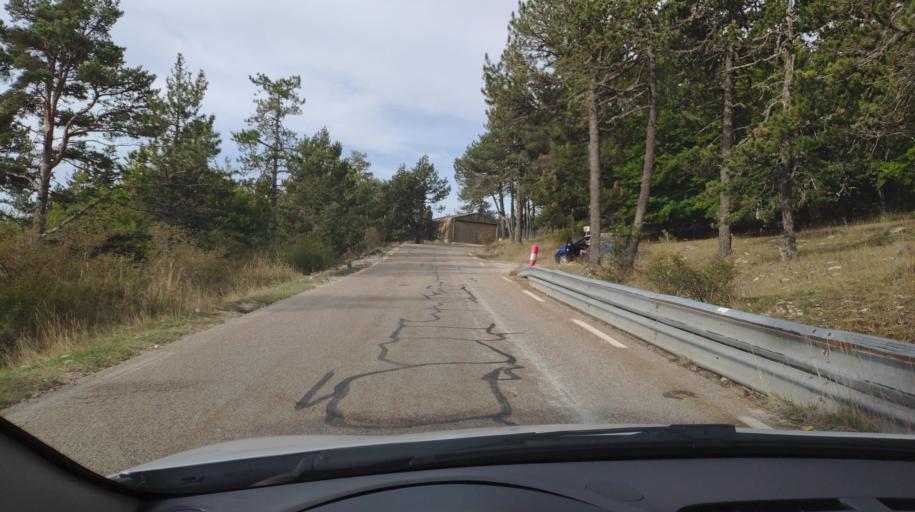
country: FR
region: Provence-Alpes-Cote d'Azur
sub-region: Departement du Vaucluse
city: Sault
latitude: 44.1459
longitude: 5.3174
